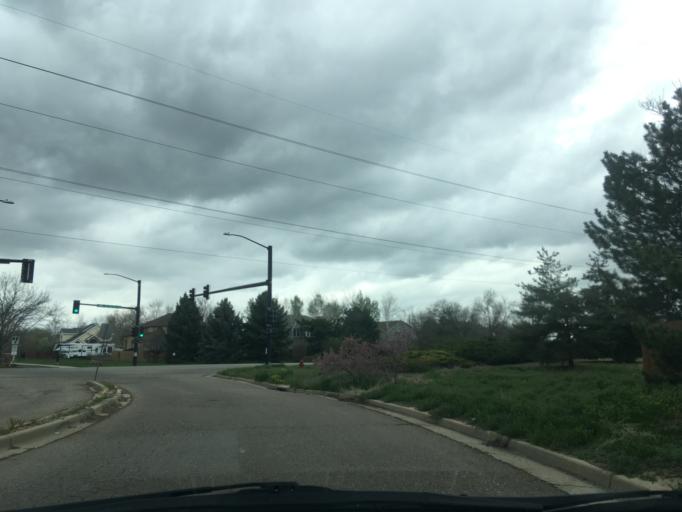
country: US
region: Colorado
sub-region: Boulder County
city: Louisville
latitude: 40.0167
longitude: -105.1305
